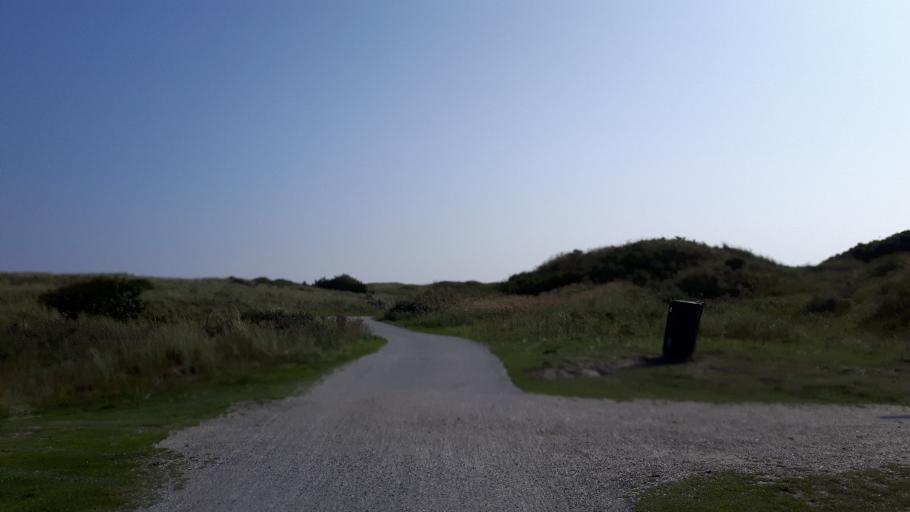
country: NL
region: Friesland
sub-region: Gemeente Ameland
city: Nes
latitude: 53.4590
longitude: 5.7912
